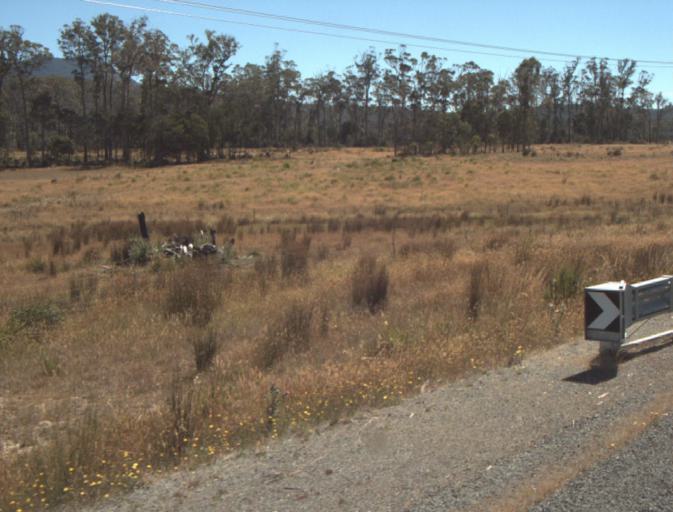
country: AU
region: Tasmania
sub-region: Launceston
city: Newstead
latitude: -41.3612
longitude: 147.3369
